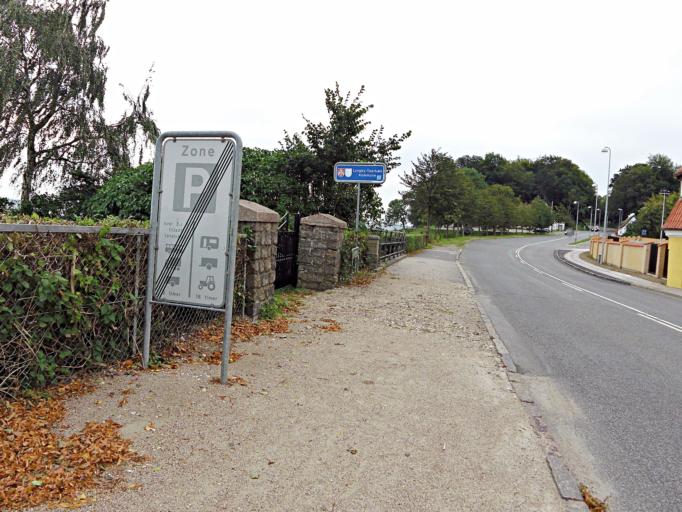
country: DK
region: Capital Region
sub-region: Rudersdal Kommune
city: Trorod
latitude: 55.8078
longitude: 12.5814
